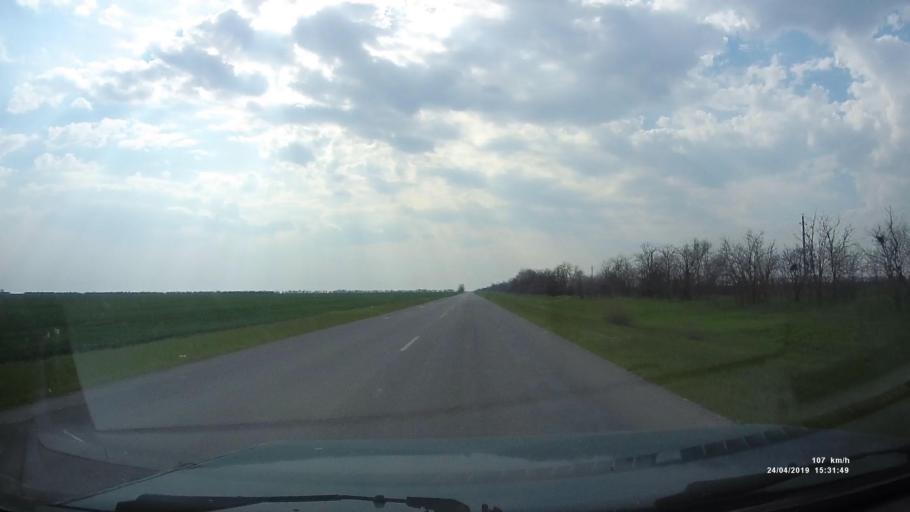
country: RU
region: Rostov
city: Remontnoye
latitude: 46.5996
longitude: 42.9747
